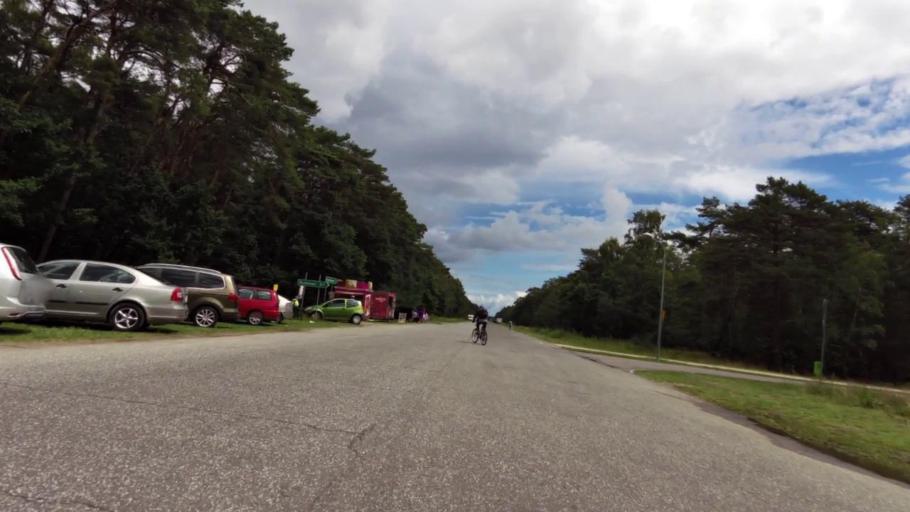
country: PL
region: West Pomeranian Voivodeship
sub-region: Powiat slawienski
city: Darlowo
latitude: 54.5207
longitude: 16.4948
